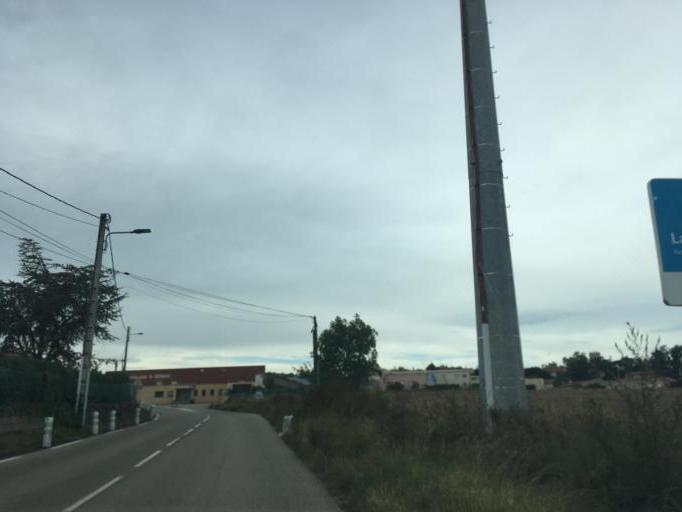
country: FR
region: Rhone-Alpes
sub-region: Departement de la Loire
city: Saint-Martin-la-Plaine
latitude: 45.5394
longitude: 4.5940
